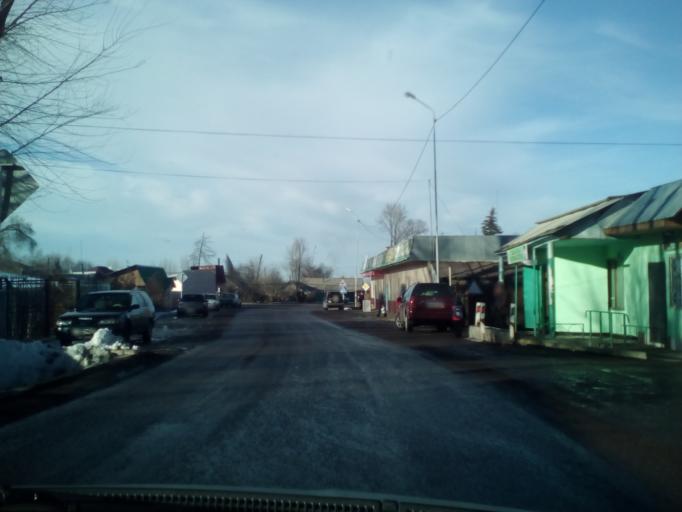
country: KZ
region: Almaty Oblysy
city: Burunday
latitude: 43.1615
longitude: 76.4164
